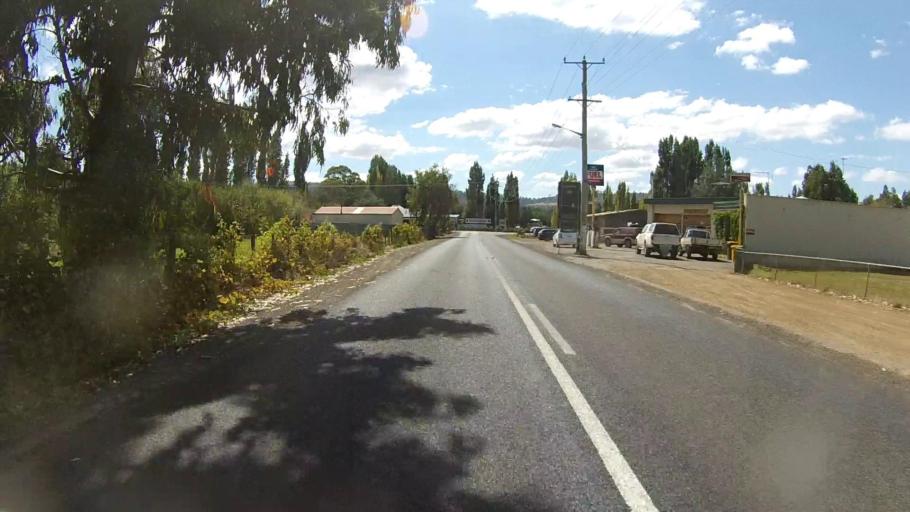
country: AU
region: Tasmania
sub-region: Derwent Valley
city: New Norfolk
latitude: -42.6750
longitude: 146.7895
